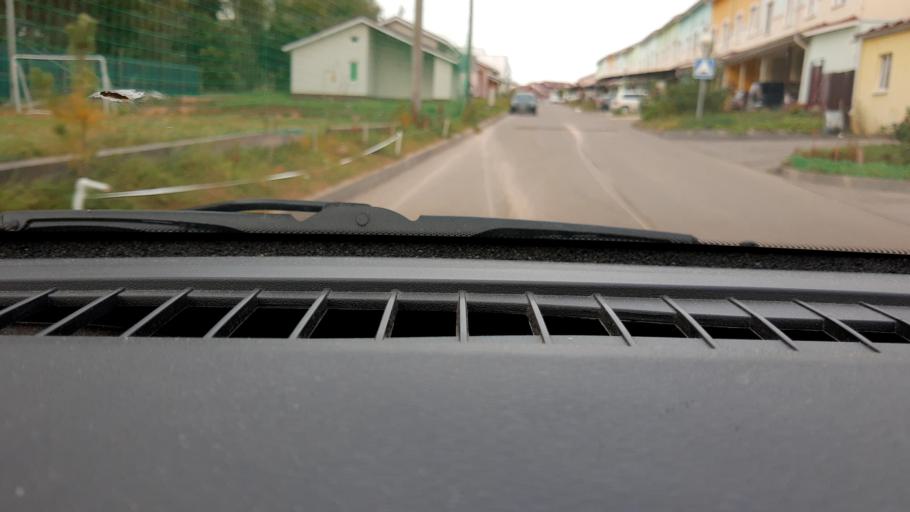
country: RU
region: Nizjnij Novgorod
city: Burevestnik
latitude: 56.0619
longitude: 43.8780
